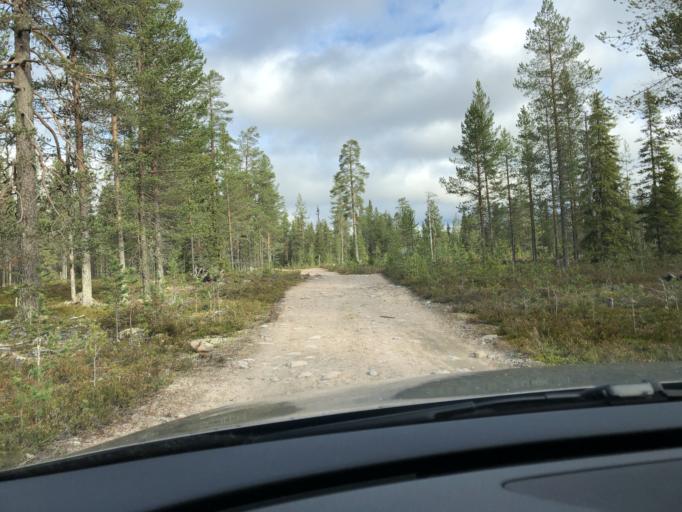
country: FI
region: Lapland
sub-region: Itae-Lappi
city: Posio
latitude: 66.0603
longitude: 27.8119
